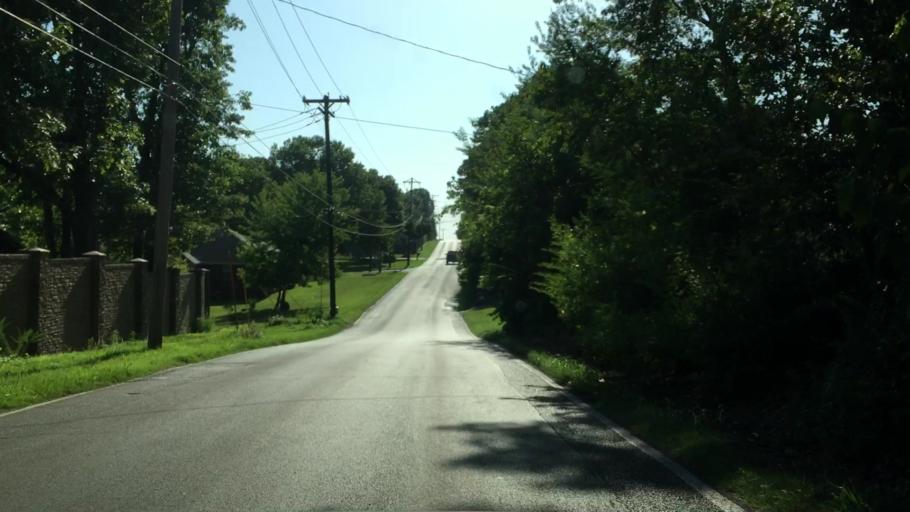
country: US
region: Oklahoma
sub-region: Cherokee County
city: Tahlequah
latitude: 35.9008
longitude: -94.9647
